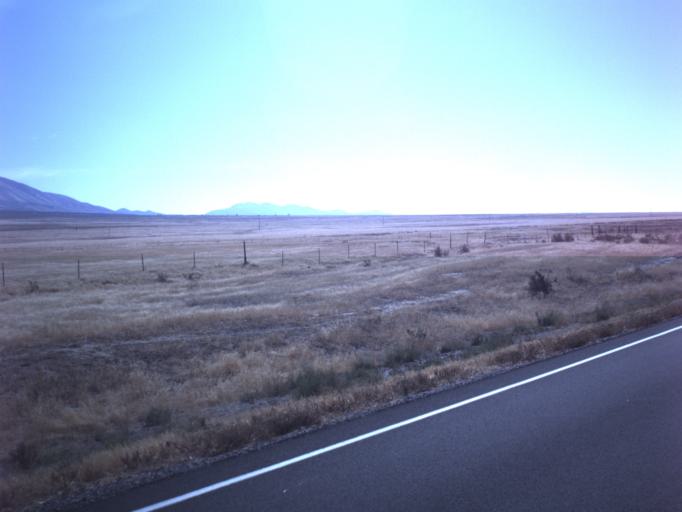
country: US
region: Utah
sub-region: Tooele County
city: Grantsville
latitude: 40.4526
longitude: -112.7481
